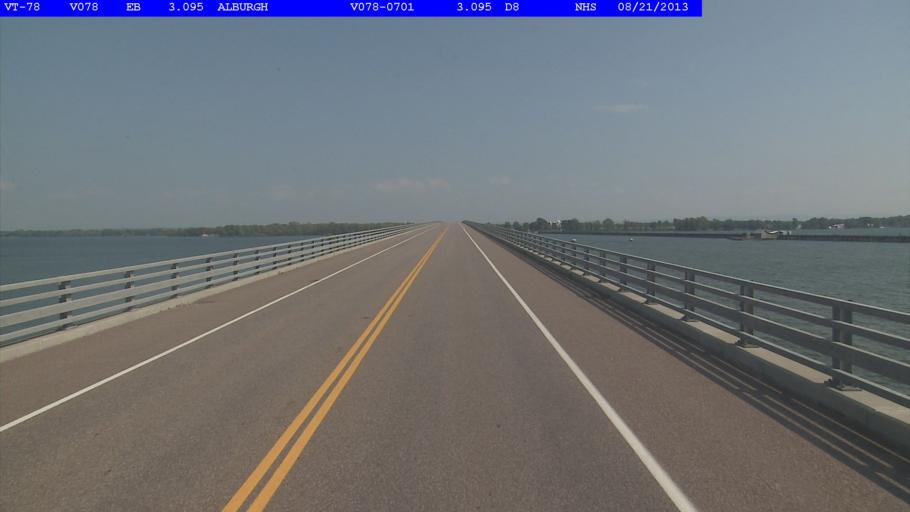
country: US
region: Vermont
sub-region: Franklin County
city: Swanton
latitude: 44.9743
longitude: -73.2249
